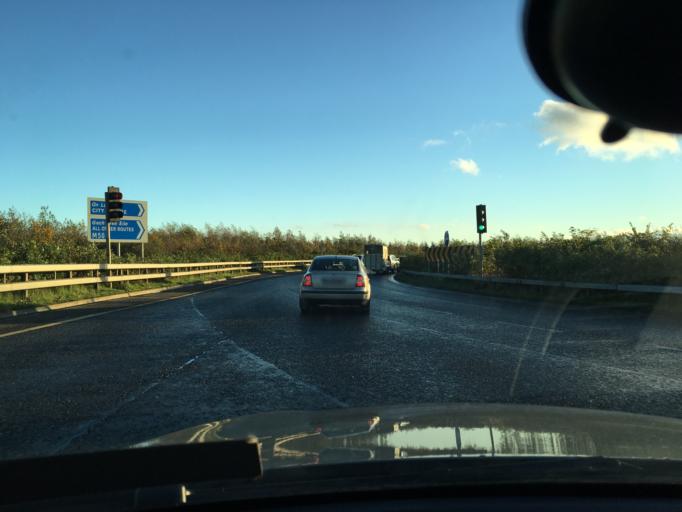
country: IE
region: Leinster
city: Kinsealy-Drinan
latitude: 53.4276
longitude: -6.2161
